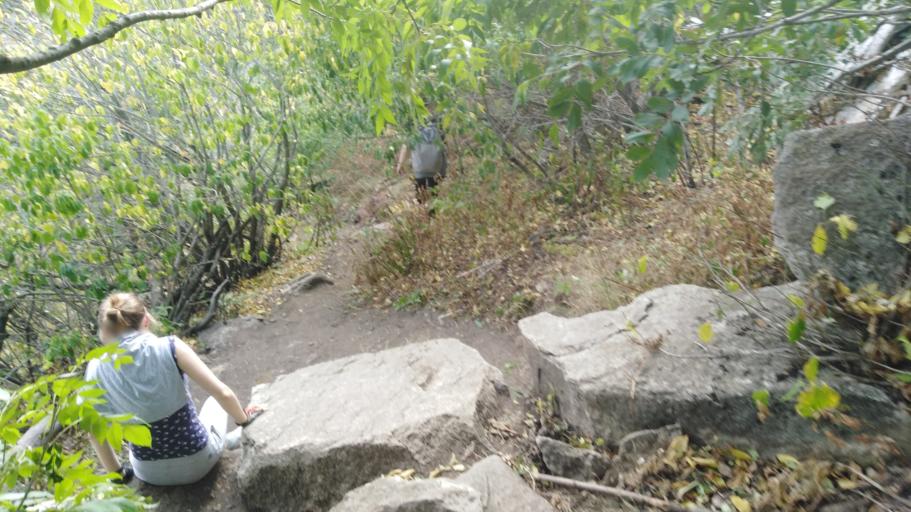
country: RU
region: Stavropol'skiy
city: Zheleznovodsk
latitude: 44.0973
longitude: 43.0273
